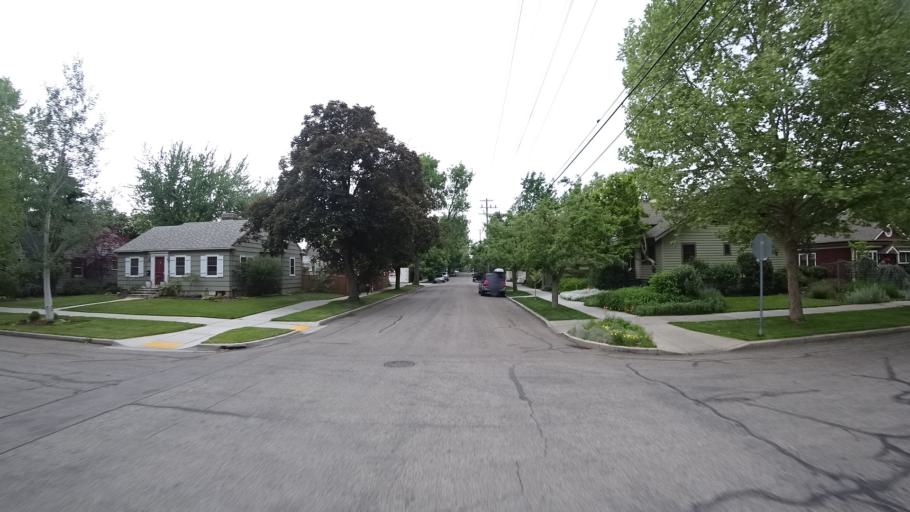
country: US
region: Idaho
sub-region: Ada County
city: Boise
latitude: 43.6088
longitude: -116.1812
